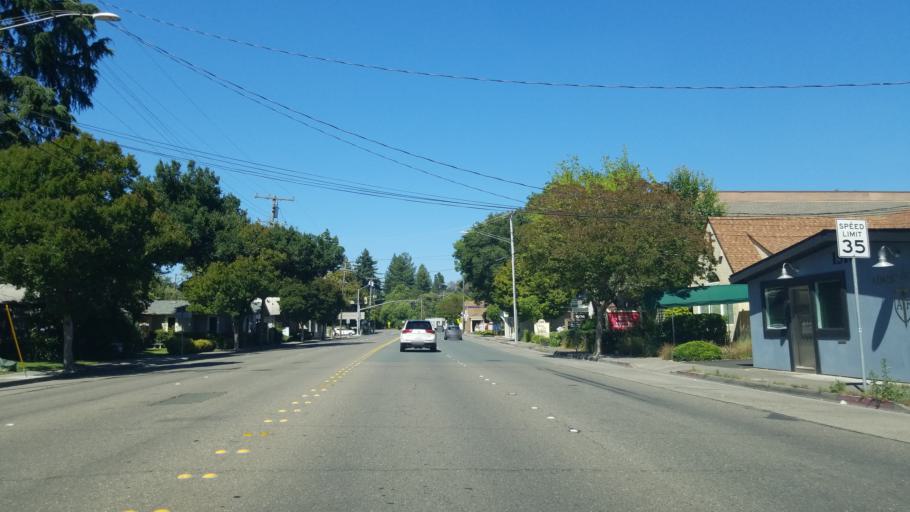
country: US
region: California
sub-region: Sonoma County
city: Santa Rosa
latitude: 38.4476
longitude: -122.7006
